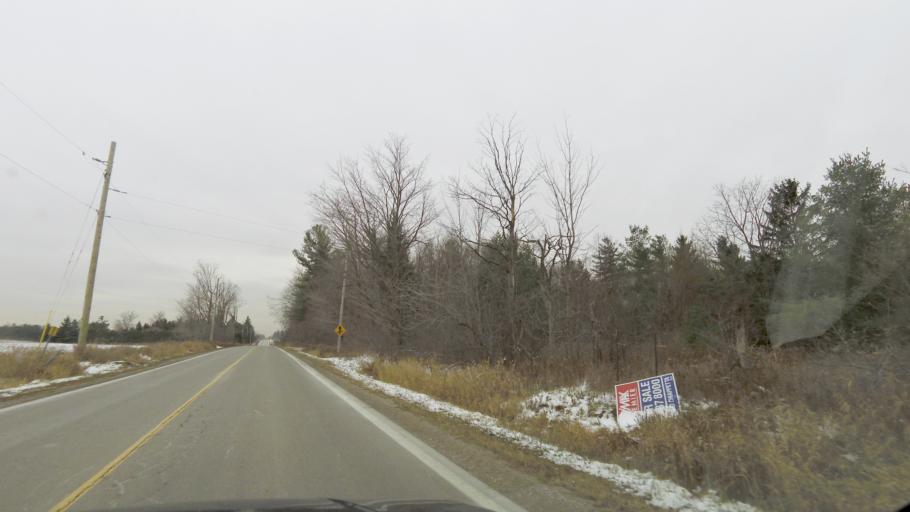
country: CA
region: Ontario
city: Vaughan
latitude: 43.8607
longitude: -79.5912
